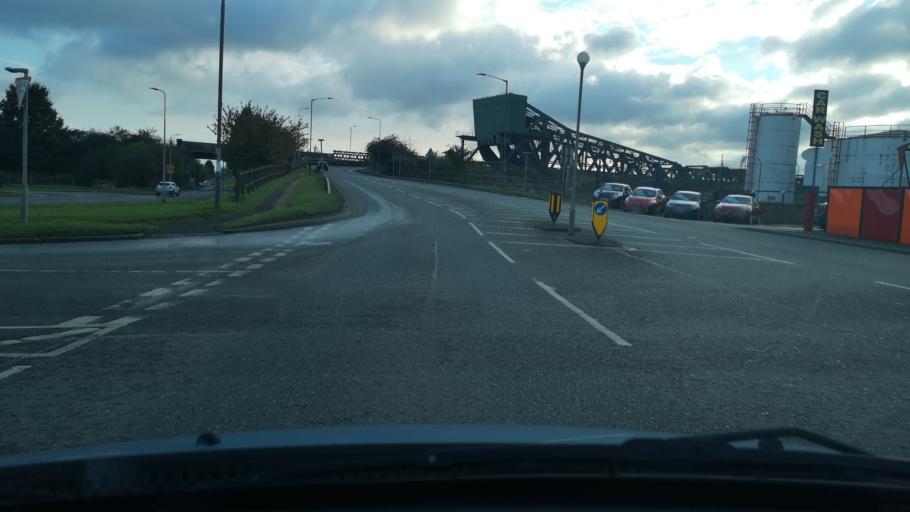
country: GB
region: England
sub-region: North Lincolnshire
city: Gunness
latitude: 53.5873
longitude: -0.7288
